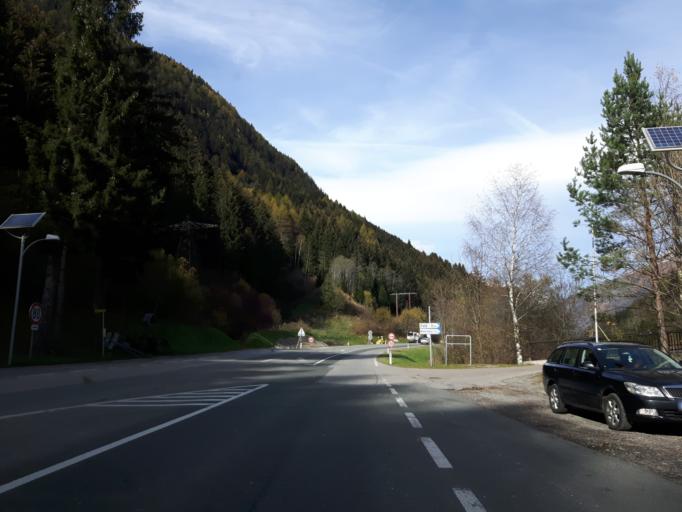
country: AT
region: Tyrol
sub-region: Politischer Bezirk Lienz
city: Hopfgarten in Defereggen
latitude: 46.9599
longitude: 12.5532
